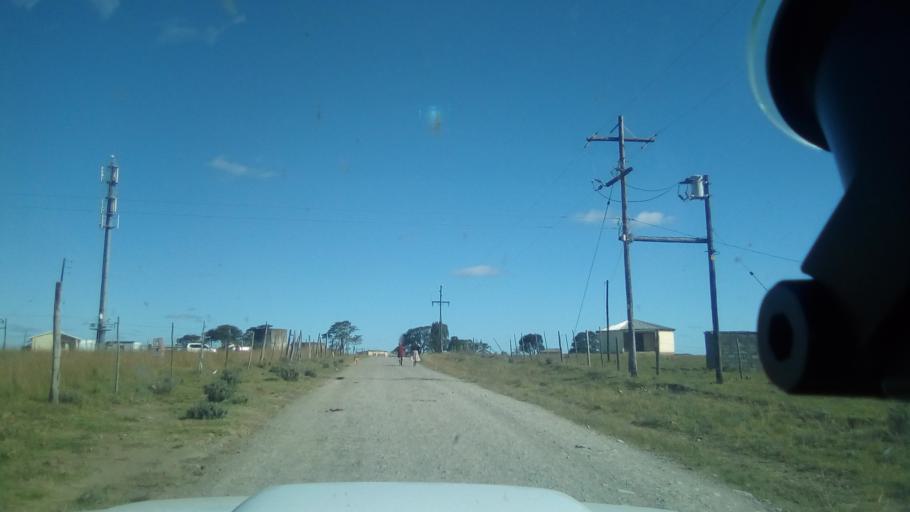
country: ZA
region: Eastern Cape
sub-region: Buffalo City Metropolitan Municipality
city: Bhisho
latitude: -32.7883
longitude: 27.3249
